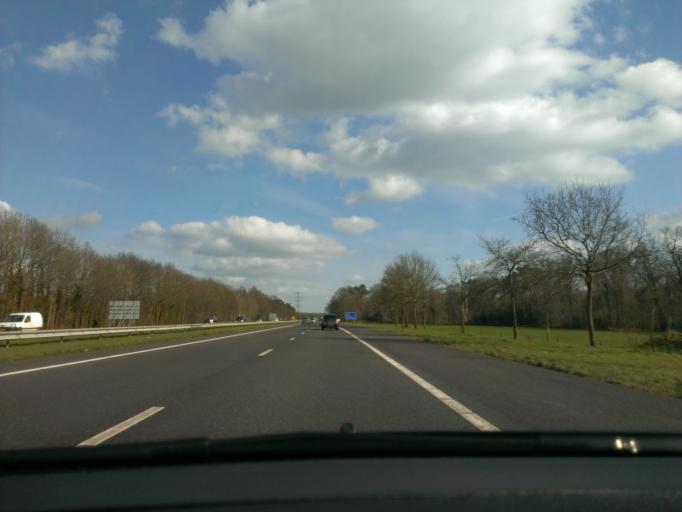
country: NL
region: Overijssel
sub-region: Gemeente Hengelo
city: Hengelo
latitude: 52.2324
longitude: 6.7735
